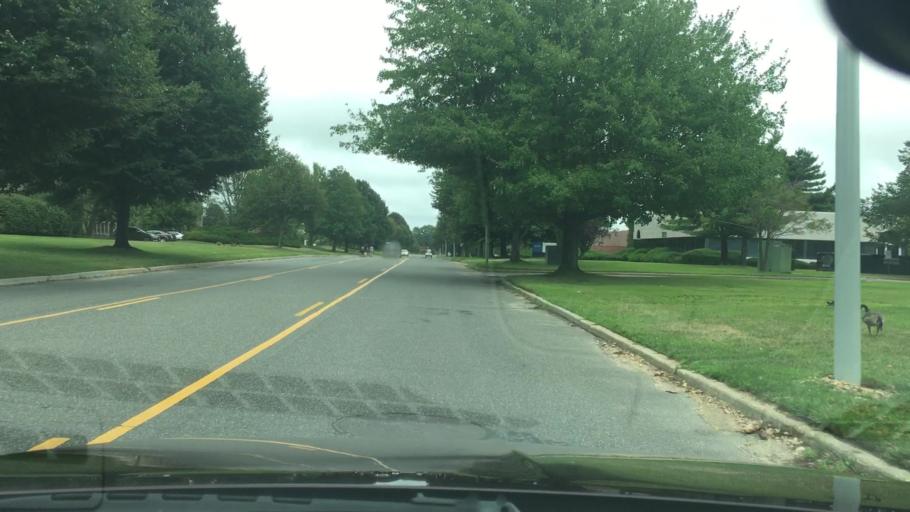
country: US
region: New York
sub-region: Suffolk County
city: Brentwood
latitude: 40.8136
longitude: -73.2638
